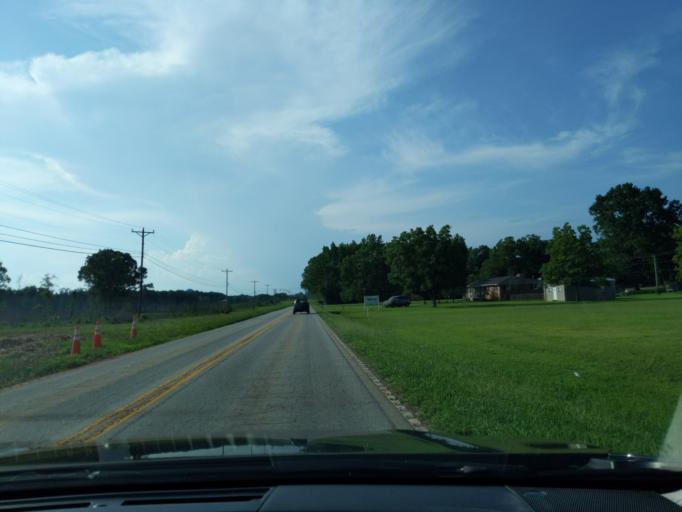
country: US
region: South Carolina
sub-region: Laurens County
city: Clinton
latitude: 34.4422
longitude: -81.8703
